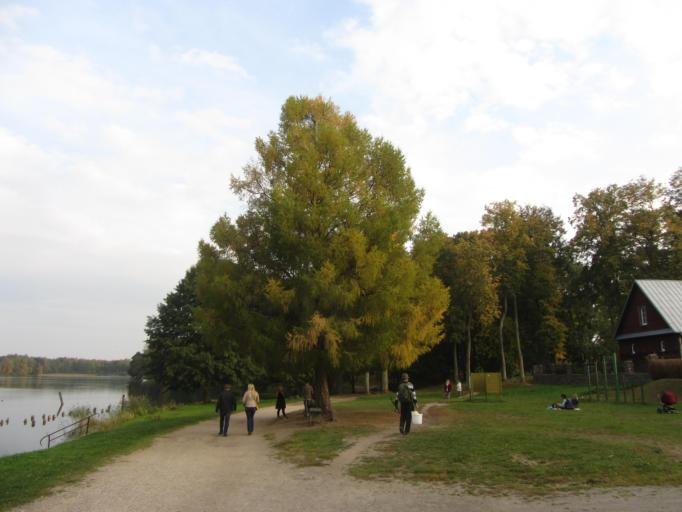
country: LT
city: Trakai
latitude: 54.6420
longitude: 24.9365
